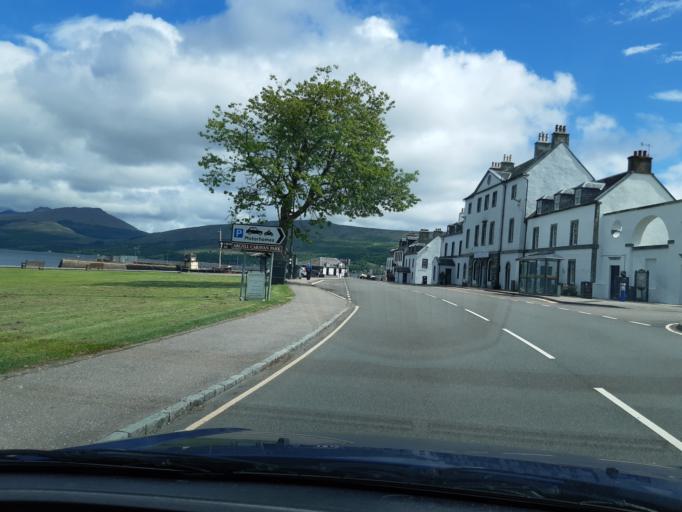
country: GB
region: Scotland
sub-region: Argyll and Bute
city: Garelochhead
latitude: 56.2318
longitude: -5.0735
